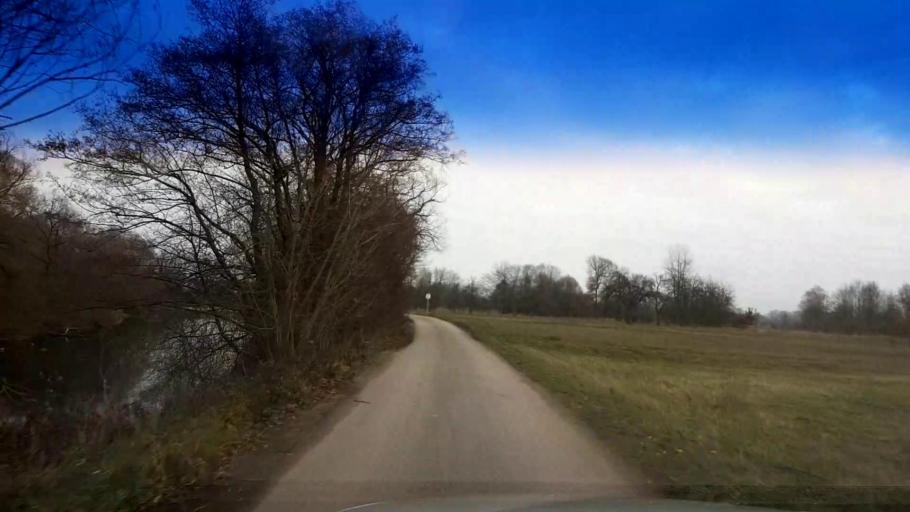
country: DE
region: Bavaria
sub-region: Upper Franconia
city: Kemmern
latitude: 49.9545
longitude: 10.8636
